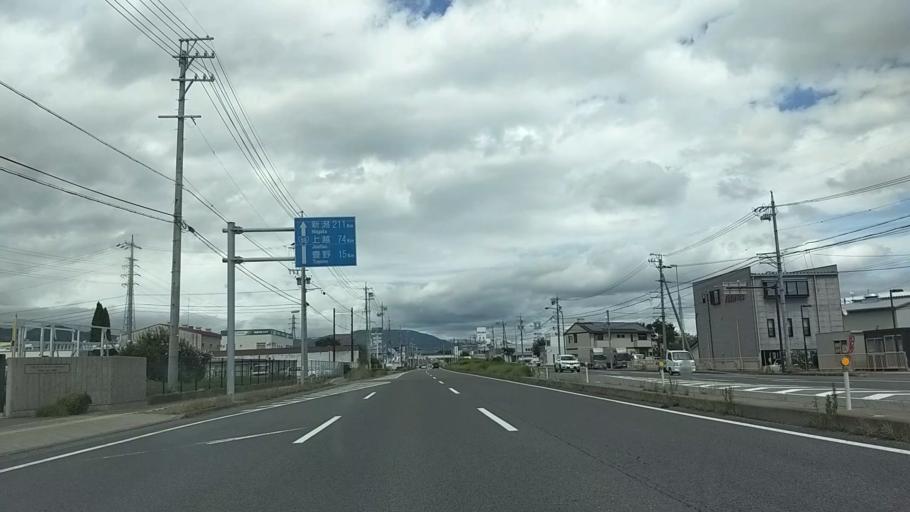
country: JP
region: Nagano
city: Nagano-shi
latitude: 36.6105
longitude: 138.1963
